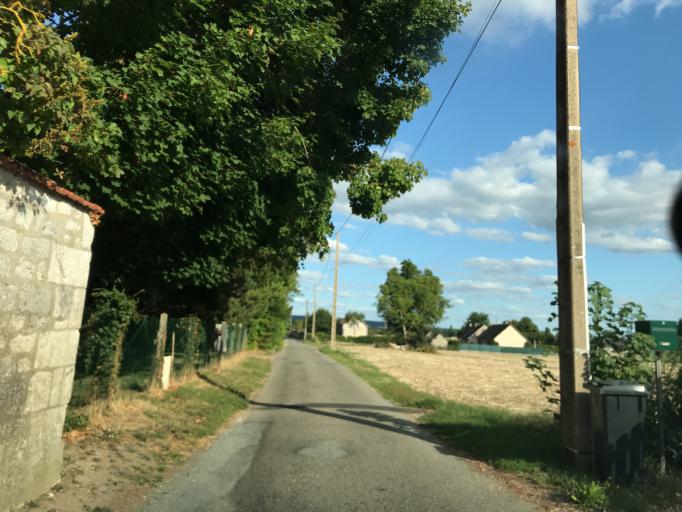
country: FR
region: Haute-Normandie
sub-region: Departement de l'Eure
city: Courcelles-sur-Seine
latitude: 49.1686
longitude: 1.4018
